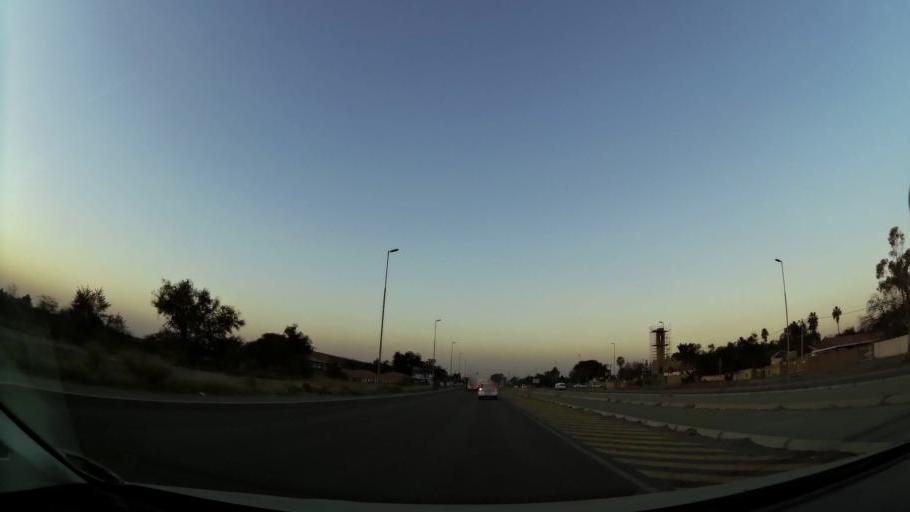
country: ZA
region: North-West
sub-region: Bojanala Platinum District Municipality
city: Rustenburg
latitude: -25.6525
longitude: 27.2480
